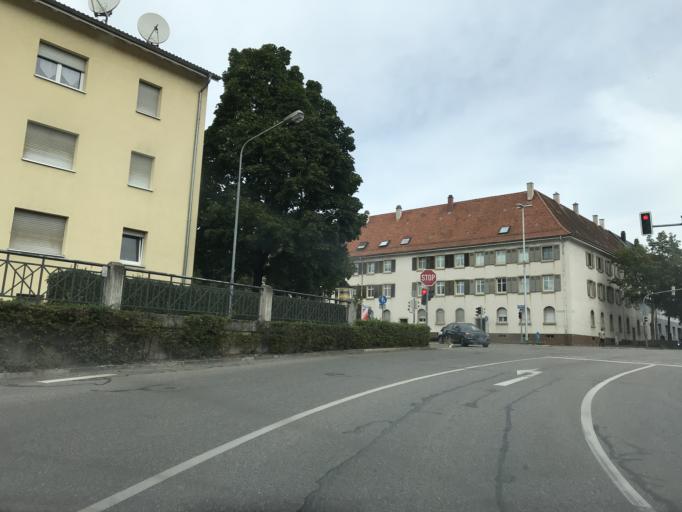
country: DE
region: Baden-Wuerttemberg
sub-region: Freiburg Region
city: Loerrach
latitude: 47.6172
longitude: 7.6664
